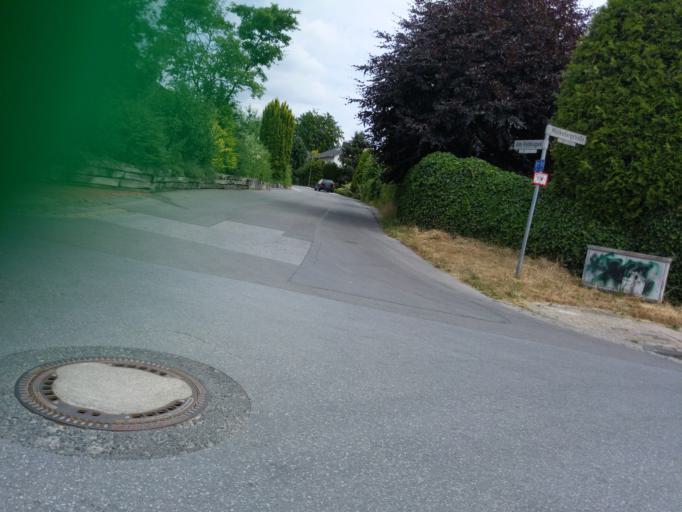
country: DE
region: North Rhine-Westphalia
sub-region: Regierungsbezirk Detmold
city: Bielefeld
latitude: 52.0265
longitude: 8.4812
